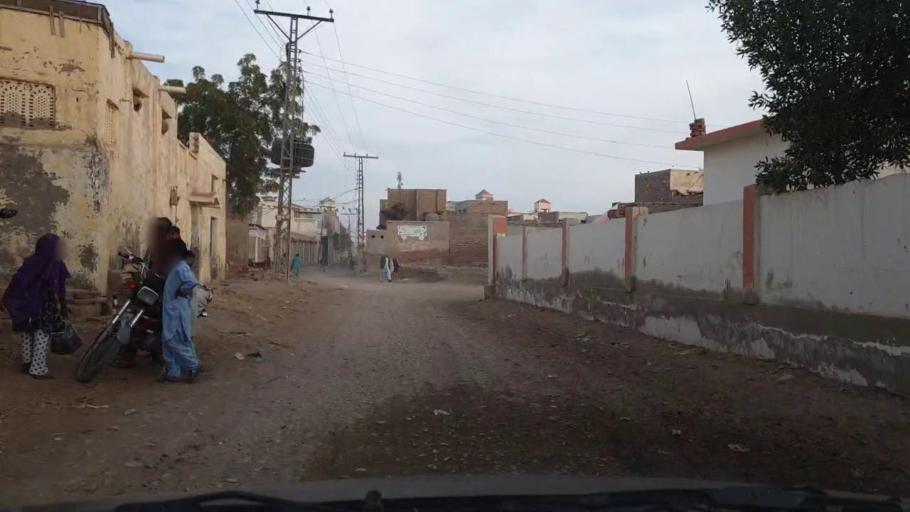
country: PK
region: Sindh
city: Khadro
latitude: 26.1491
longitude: 68.7152
